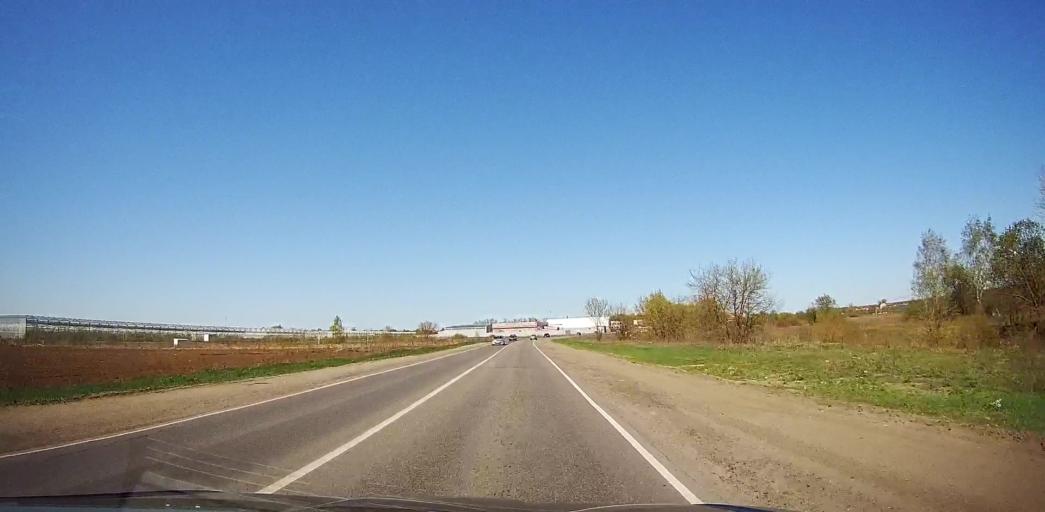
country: RU
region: Moskovskaya
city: Ramenskoye
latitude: 55.5365
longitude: 38.2782
